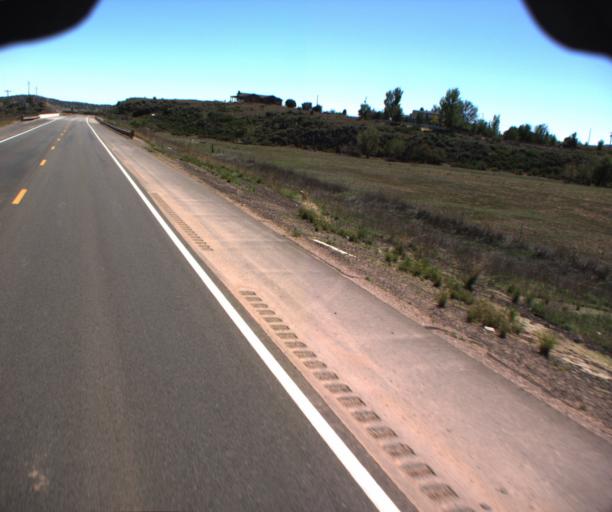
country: US
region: Arizona
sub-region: Yavapai County
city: Paulden
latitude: 34.8720
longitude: -112.4697
